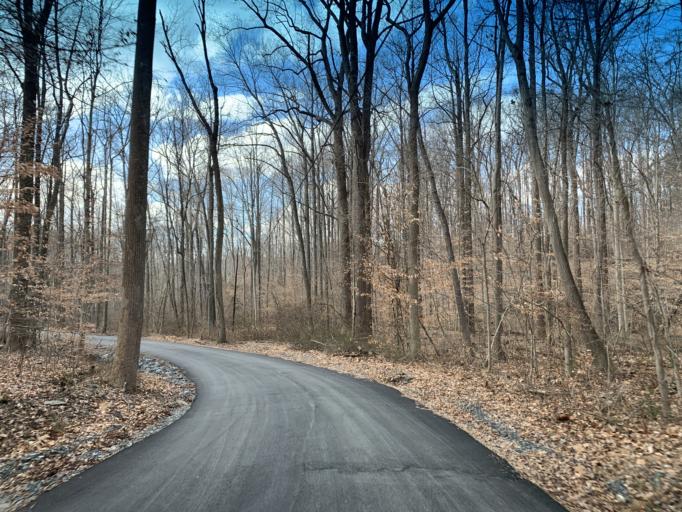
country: US
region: Maryland
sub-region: Harford County
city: Riverside
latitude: 39.5034
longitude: -76.2546
